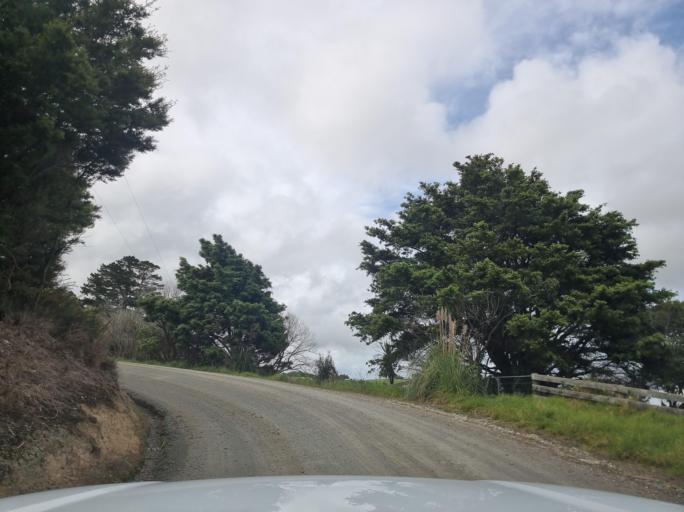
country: NZ
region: Northland
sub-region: Whangarei
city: Ruakaka
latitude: -36.1100
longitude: 174.2109
